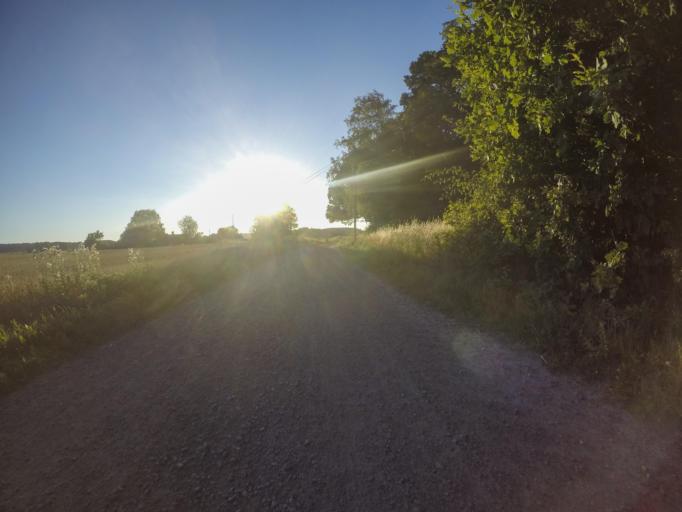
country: SE
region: Vaestmanland
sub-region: Vasteras
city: Vasteras
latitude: 59.5676
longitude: 16.6537
